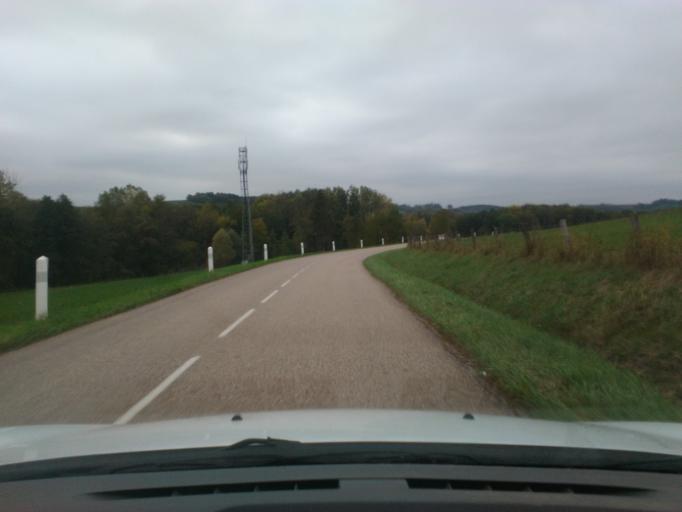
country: FR
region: Lorraine
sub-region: Departement des Vosges
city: Vincey
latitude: 48.2970
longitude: 6.2991
